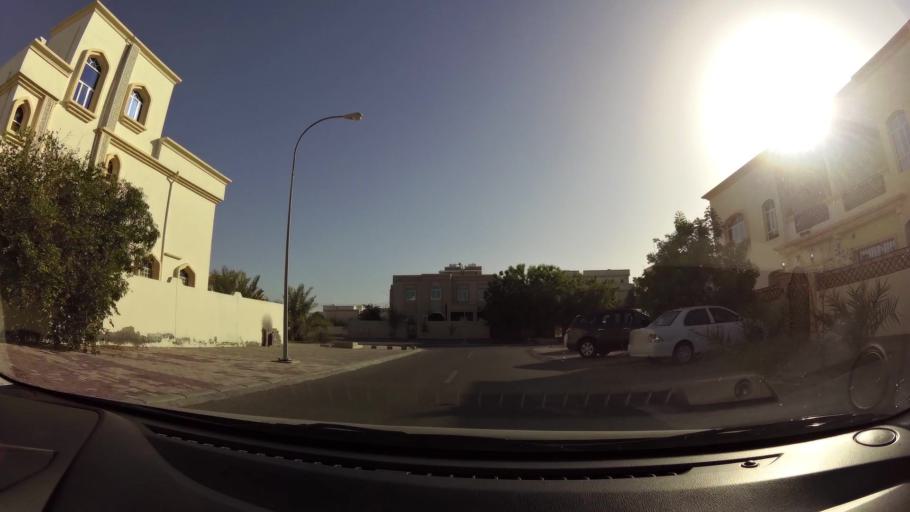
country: OM
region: Muhafazat Masqat
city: As Sib al Jadidah
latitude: 23.5990
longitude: 58.2076
